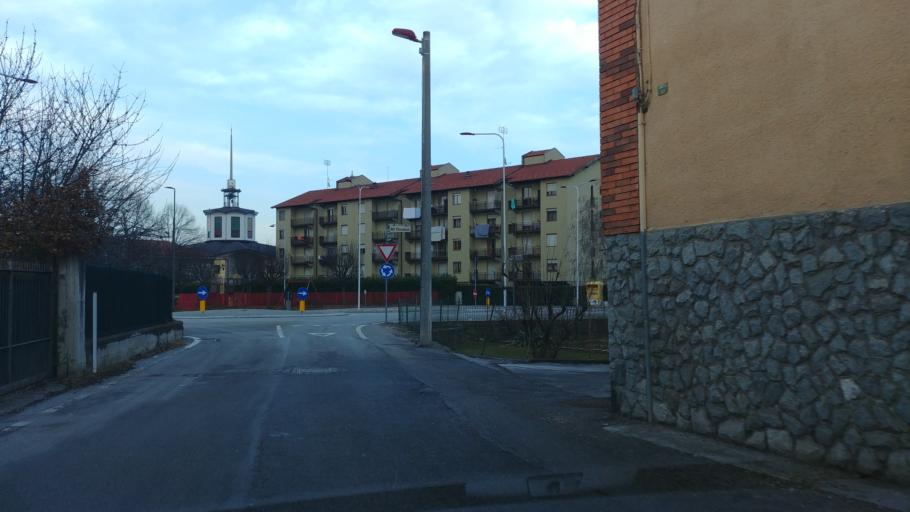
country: IT
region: Piedmont
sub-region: Provincia di Cuneo
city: Cuneo
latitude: 44.4003
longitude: 7.5308
